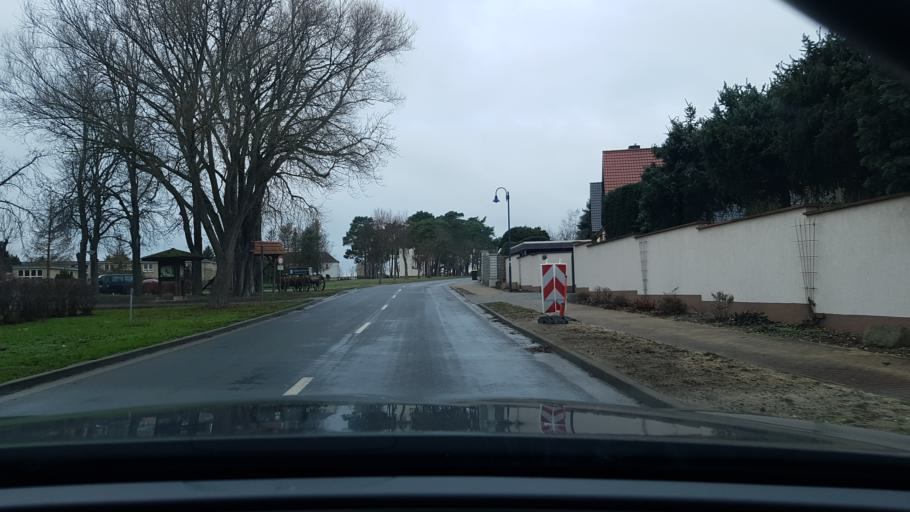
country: DE
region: Saxony-Anhalt
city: Weferlingen
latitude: 52.4036
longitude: 11.1087
